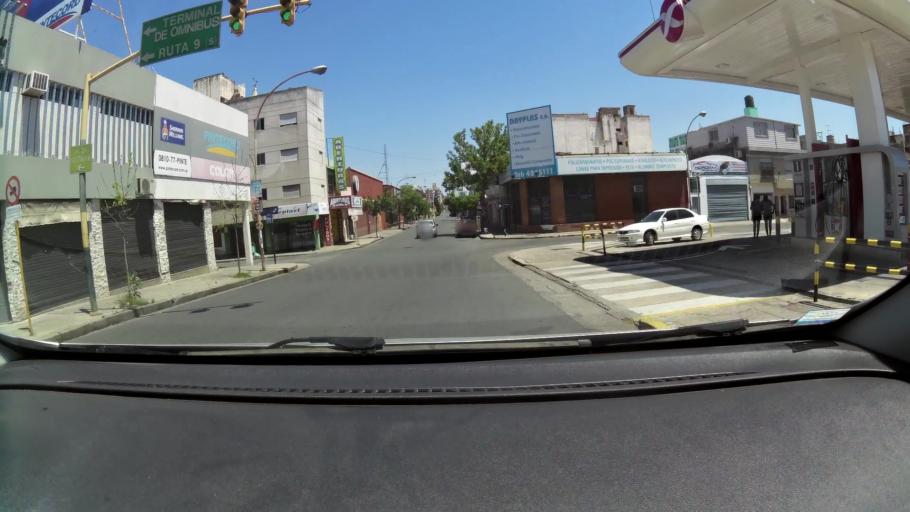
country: AR
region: Cordoba
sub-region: Departamento de Capital
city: Cordoba
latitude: -31.4074
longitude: -64.1775
